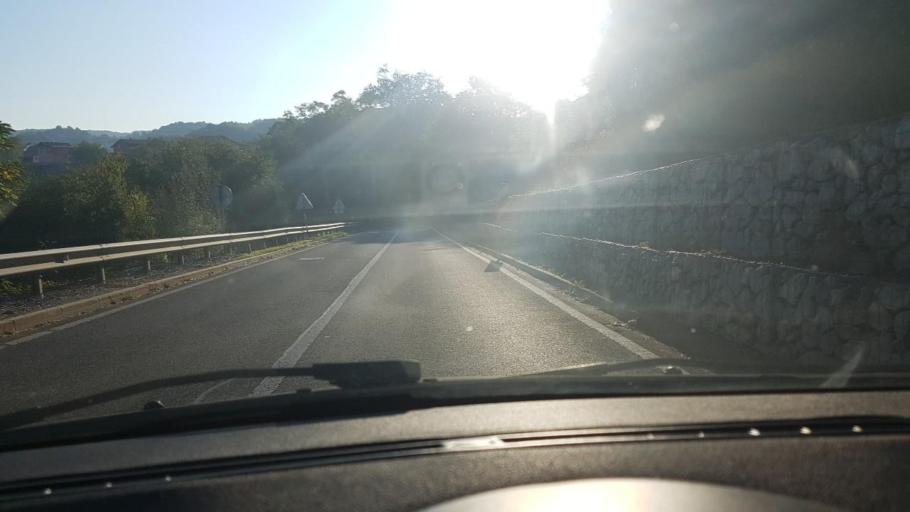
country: HR
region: Krapinsko-Zagorska
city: Marija Bistrica
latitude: 45.9718
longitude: 16.1003
